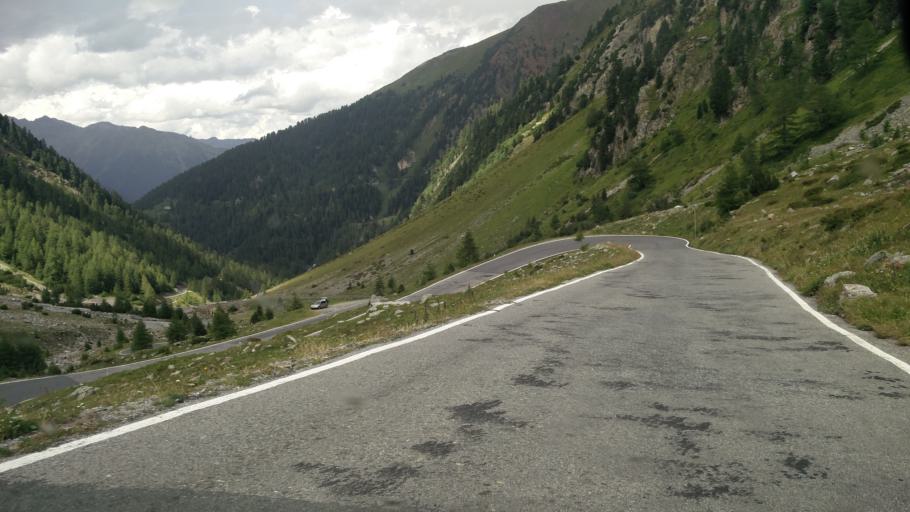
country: IT
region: Trentino-Alto Adige
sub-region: Bolzano
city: Tubre
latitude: 46.5660
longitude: 10.4371
